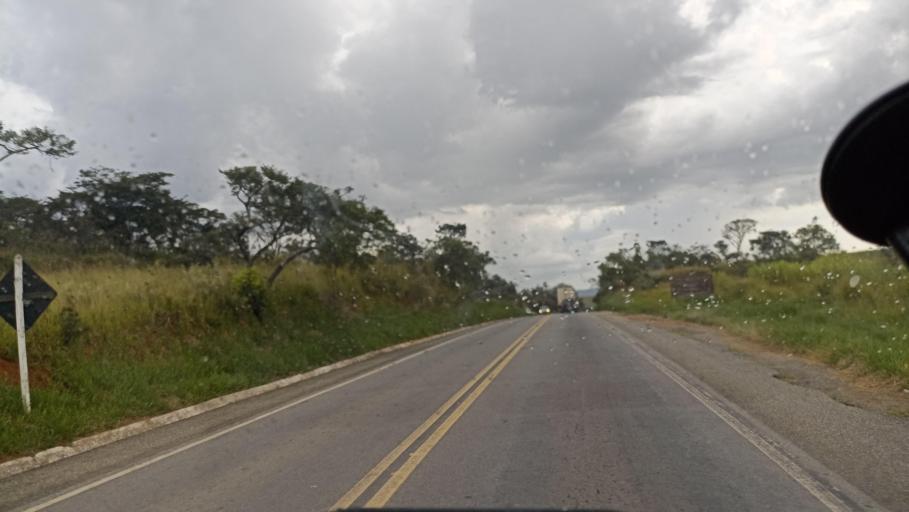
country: BR
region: Minas Gerais
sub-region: Baependi
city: Baependi
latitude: -21.9252
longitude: -44.8248
